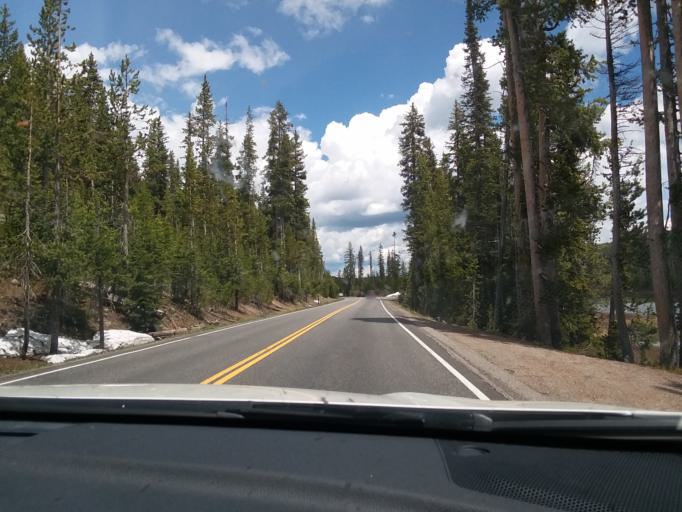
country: US
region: Montana
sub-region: Gallatin County
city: West Yellowstone
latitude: 44.2455
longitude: -110.6466
